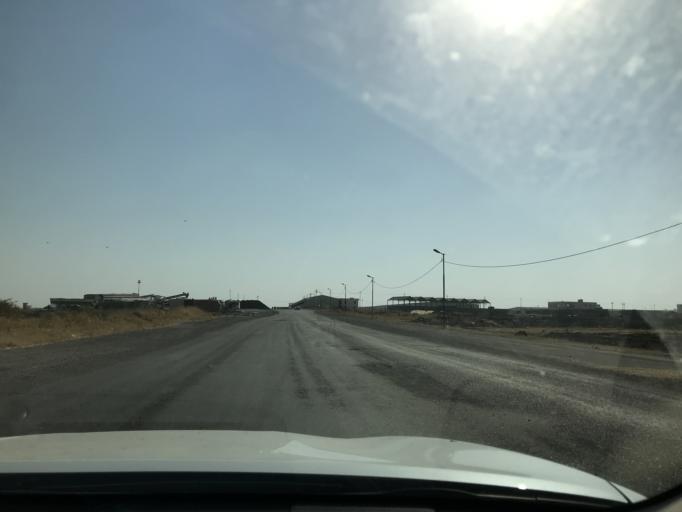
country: IQ
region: Arbil
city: Erbil
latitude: 36.1703
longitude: 43.9210
